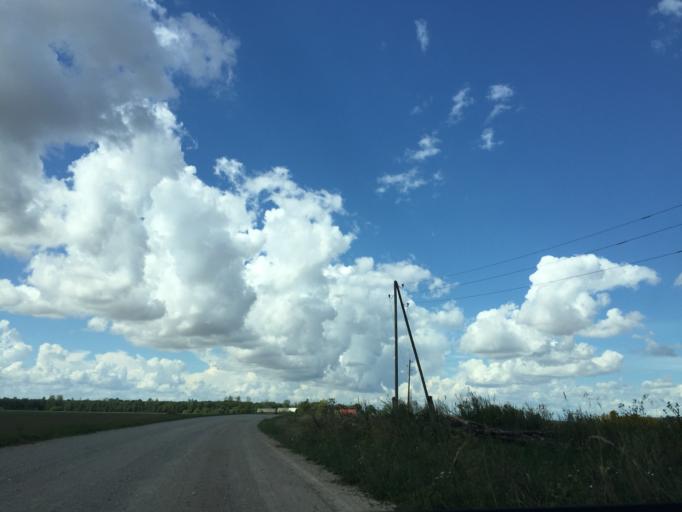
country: LV
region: Rundales
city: Pilsrundale
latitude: 56.3531
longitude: 23.9756
